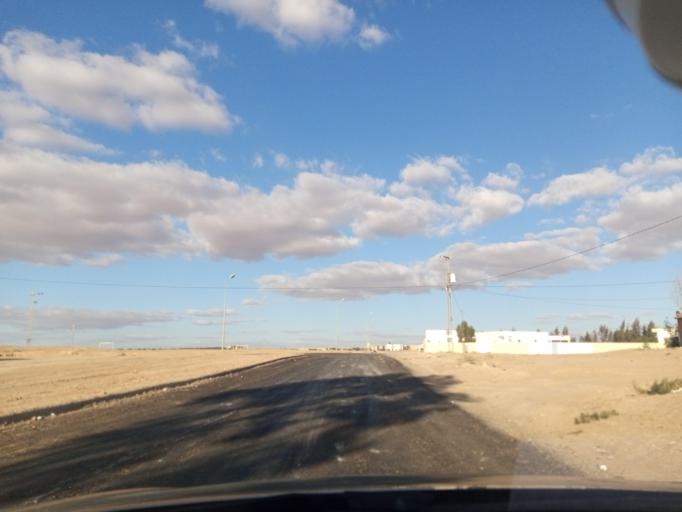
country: TN
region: Safaqis
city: Bi'r `Ali Bin Khalifah
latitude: 34.7129
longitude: 10.4224
